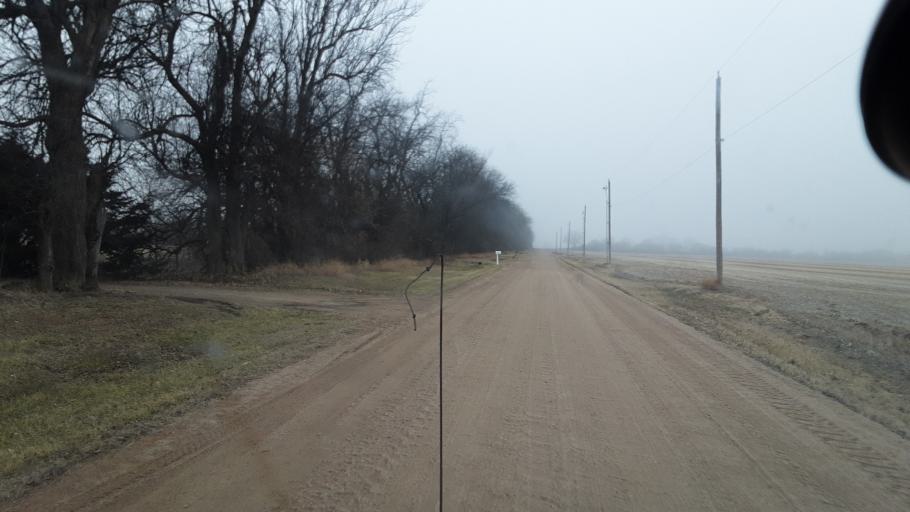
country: US
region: Kansas
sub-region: Reno County
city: South Hutchinson
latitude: 37.9555
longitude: -97.9425
